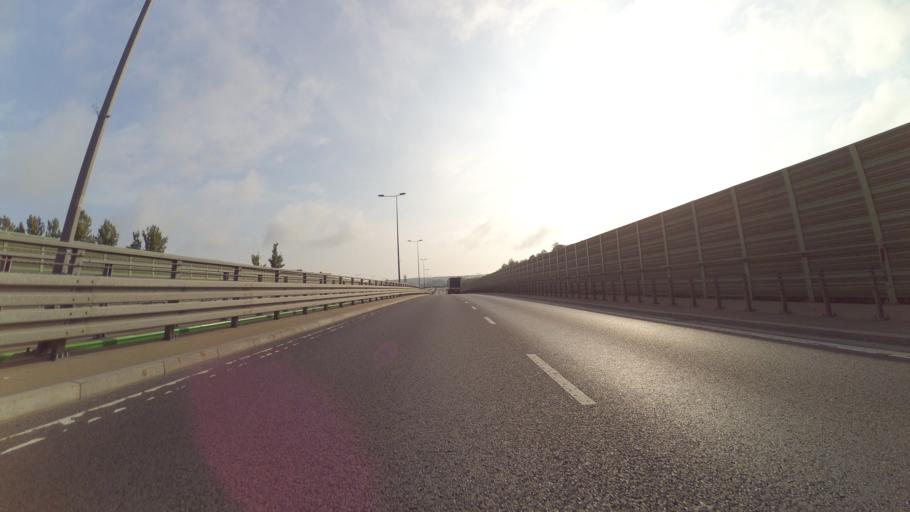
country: PL
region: Podlasie
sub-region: Bialystok
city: Bialystok
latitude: 53.1554
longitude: 23.0870
